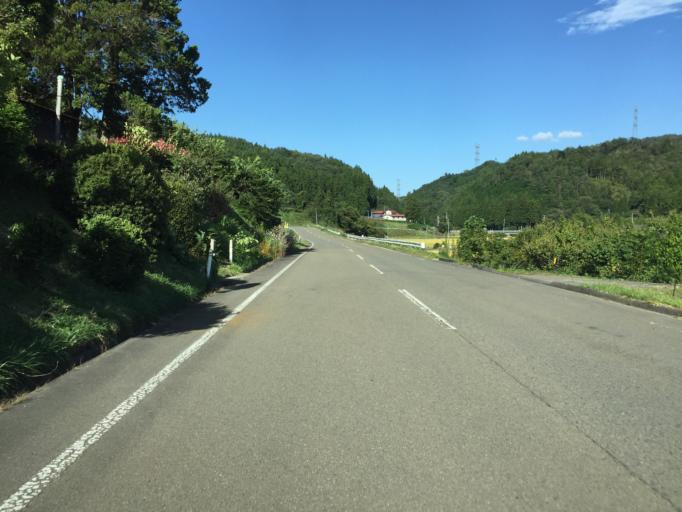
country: JP
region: Miyagi
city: Marumori
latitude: 37.8415
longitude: 140.7363
